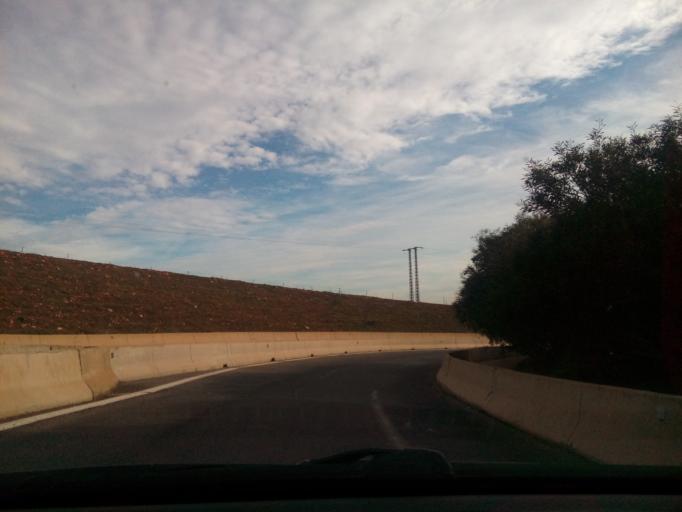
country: DZ
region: Oran
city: Sidi ech Chahmi
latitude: 35.5453
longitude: -0.3795
